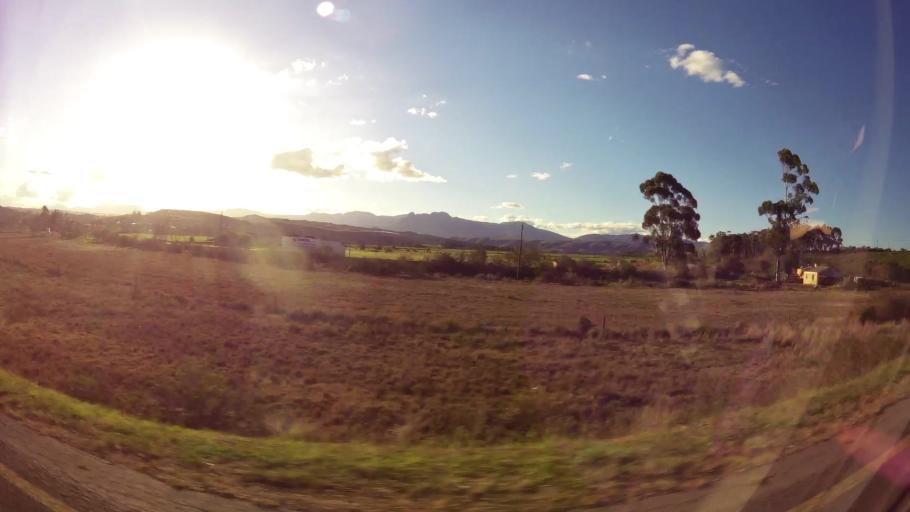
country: ZA
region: Western Cape
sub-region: Eden District Municipality
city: Riversdale
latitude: -34.0929
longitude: 20.9737
